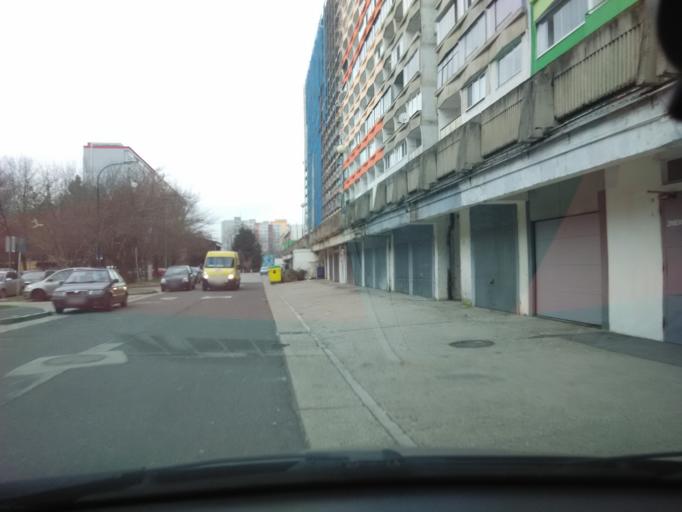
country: AT
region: Burgenland
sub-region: Politischer Bezirk Neusiedl am See
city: Kittsee
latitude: 48.1029
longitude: 17.1058
